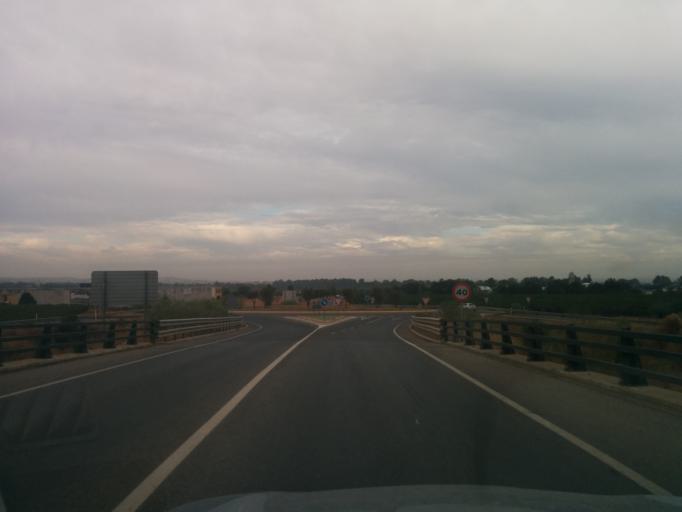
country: ES
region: Andalusia
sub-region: Provincia de Sevilla
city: La Rinconada
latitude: 37.4540
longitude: -5.9703
